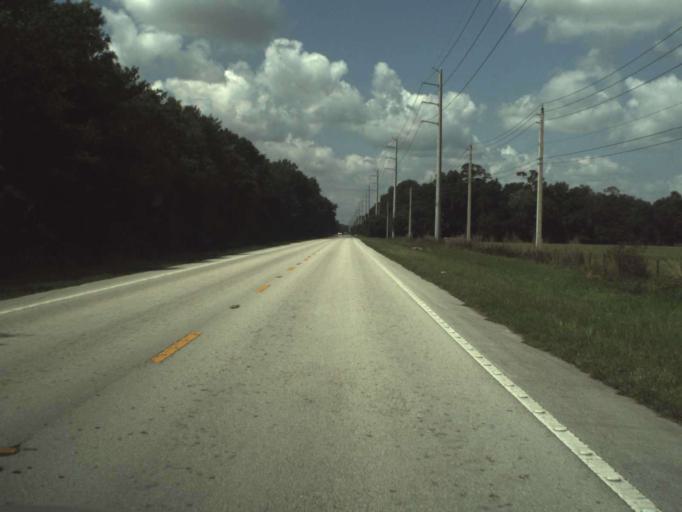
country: US
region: Florida
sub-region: Volusia County
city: Lake Helen
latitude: 28.9037
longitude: -81.1313
